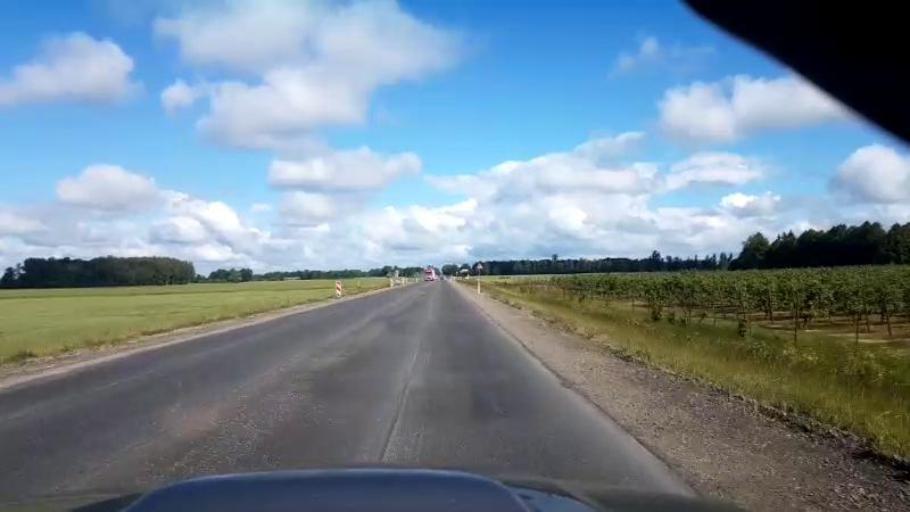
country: LV
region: Bauskas Rajons
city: Bauska
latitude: 56.3707
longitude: 24.2721
